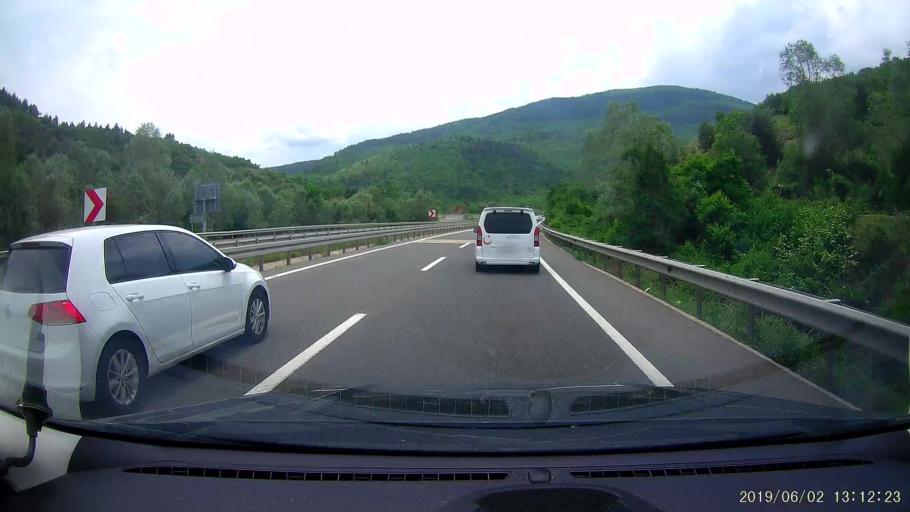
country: TR
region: Karabuk
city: Gozyeri
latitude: 40.8609
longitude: 32.6360
